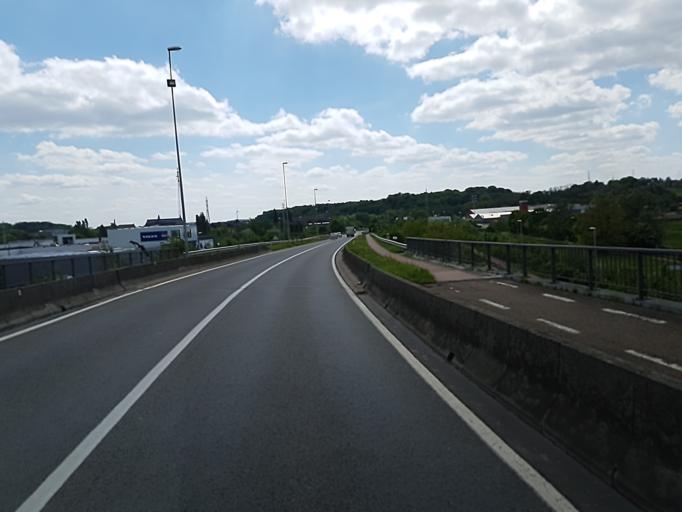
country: BE
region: Flanders
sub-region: Provincie Vlaams-Brabant
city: Diest
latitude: 50.9941
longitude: 5.0402
